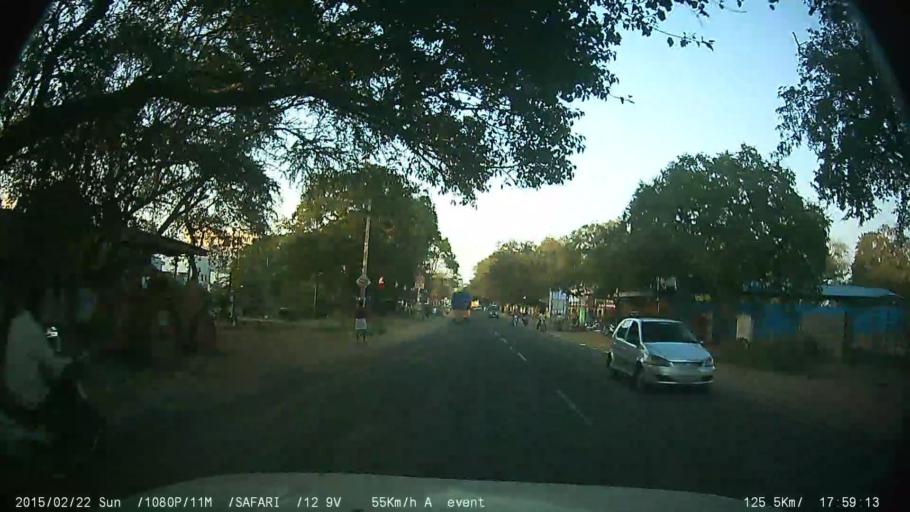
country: IN
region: Tamil Nadu
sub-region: Theni
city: Uttamapalaiyam
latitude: 9.7996
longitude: 77.3276
